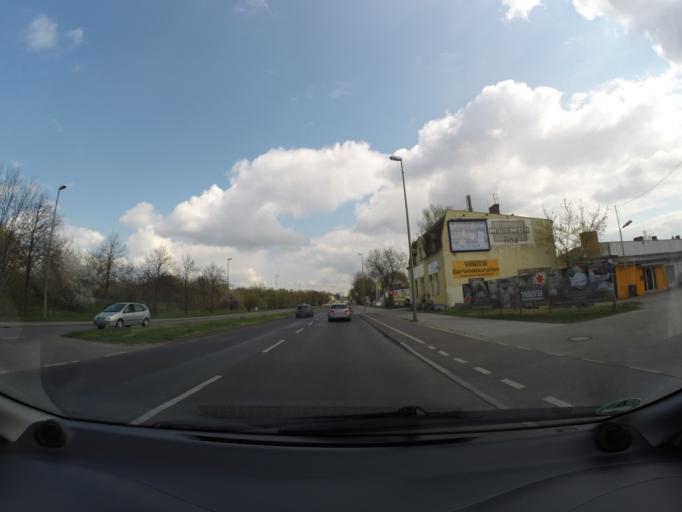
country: DE
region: Berlin
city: Mahlsdorf
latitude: 52.5198
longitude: 13.6241
